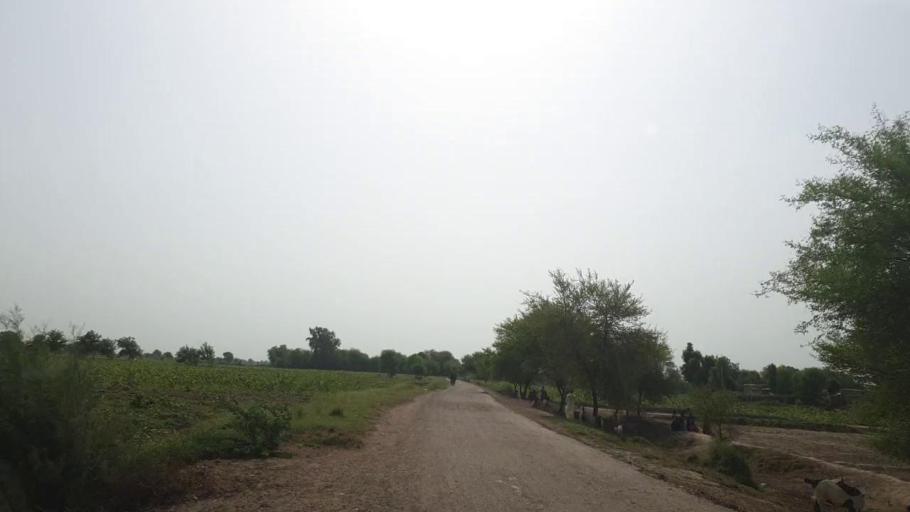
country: PK
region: Sindh
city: Nawabshah
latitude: 26.1153
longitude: 68.4311
